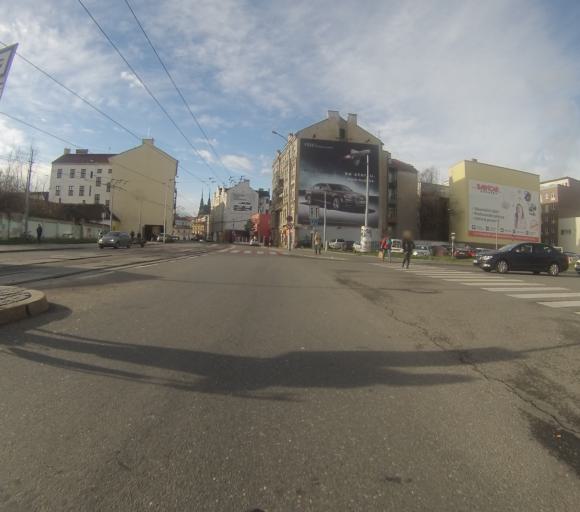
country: CZ
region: South Moravian
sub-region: Mesto Brno
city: Brno
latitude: 49.1921
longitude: 16.6182
